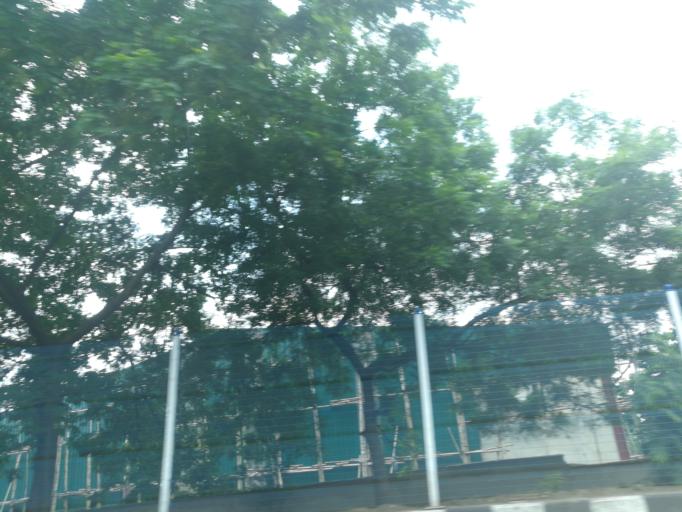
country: NG
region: Lagos
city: Ojota
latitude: 6.5953
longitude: 3.3824
